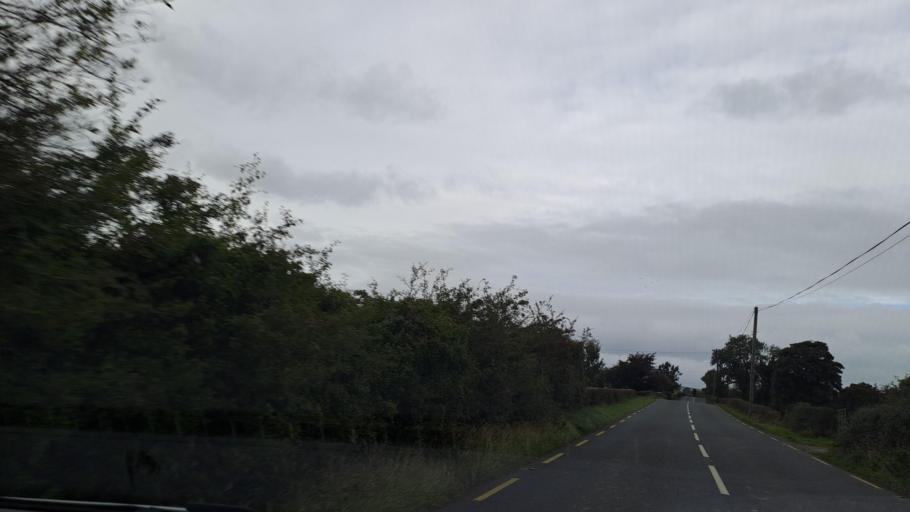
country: IE
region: Ulster
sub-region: An Cabhan
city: Bailieborough
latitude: 54.0238
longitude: -6.9062
